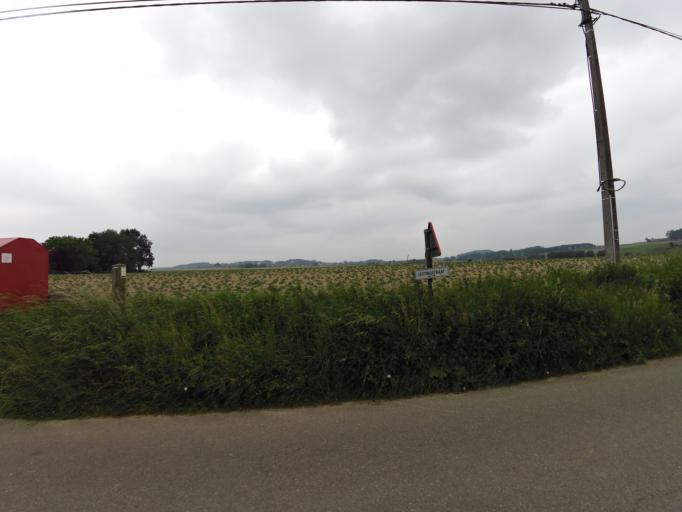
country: FR
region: Nord-Pas-de-Calais
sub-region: Departement du Nord
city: Bailleul
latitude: 50.7682
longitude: 2.7867
